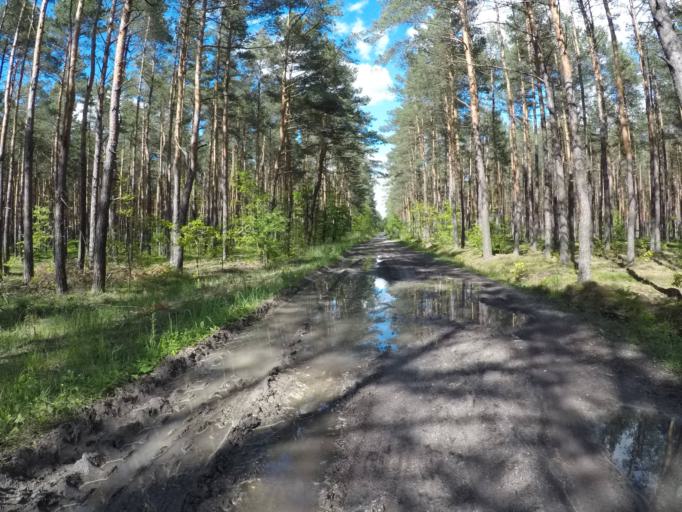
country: PL
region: Swietokrzyskie
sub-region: Powiat kielecki
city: Kostomloty Drugie
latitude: 50.8919
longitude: 20.5412
